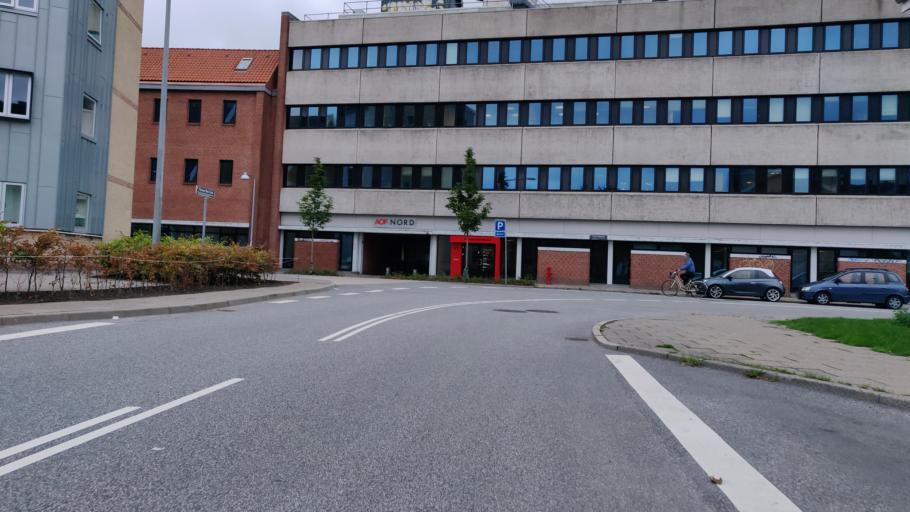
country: DK
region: North Denmark
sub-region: Alborg Kommune
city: Aalborg
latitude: 57.0444
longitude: 9.9287
